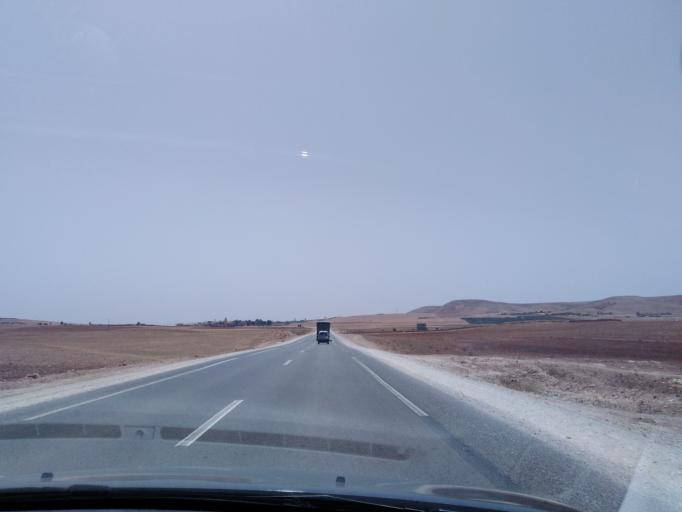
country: MA
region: Doukkala-Abda
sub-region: Safi
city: Youssoufia
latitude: 32.1169
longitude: -8.7896
